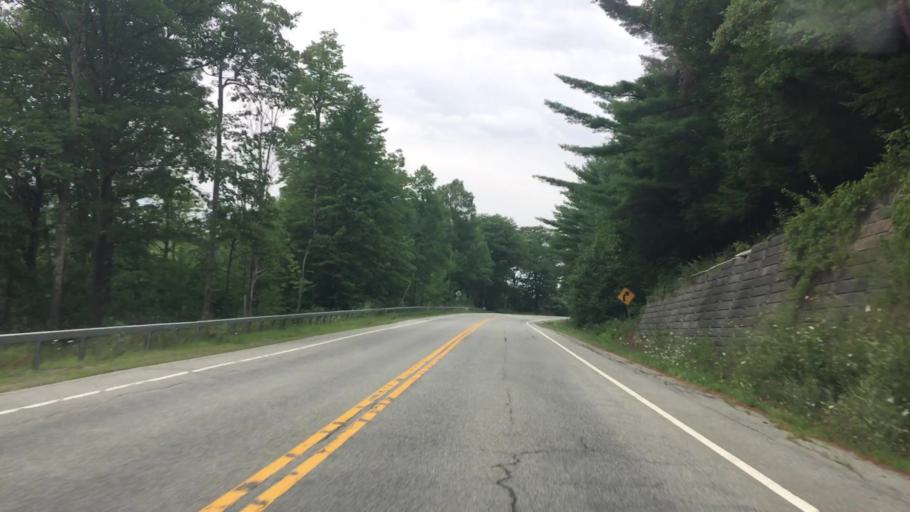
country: US
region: New York
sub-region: Essex County
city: Lake Placid
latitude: 44.2844
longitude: -73.7875
